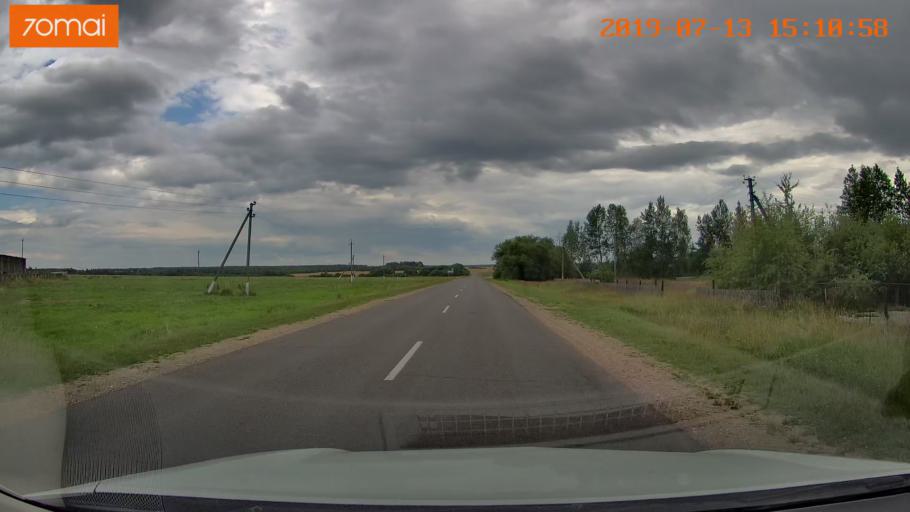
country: BY
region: Mogilev
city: Hlusha
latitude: 53.1670
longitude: 28.7807
